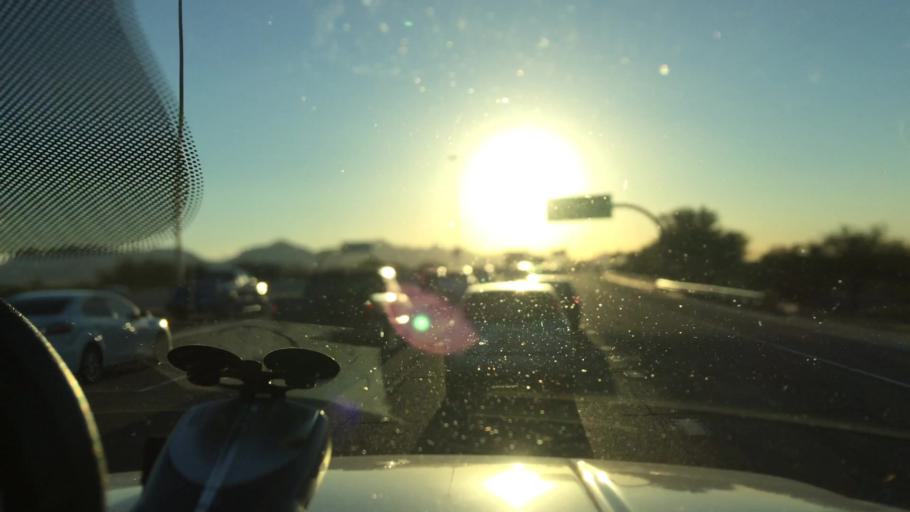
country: US
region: Arizona
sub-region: Maricopa County
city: Paradise Valley
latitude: 33.6713
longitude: -111.9695
